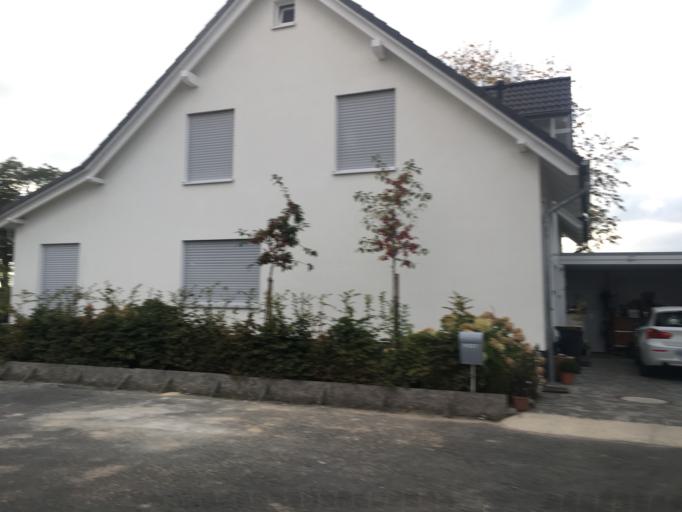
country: DE
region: North Rhine-Westphalia
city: Olfen
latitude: 51.7634
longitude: 7.3857
